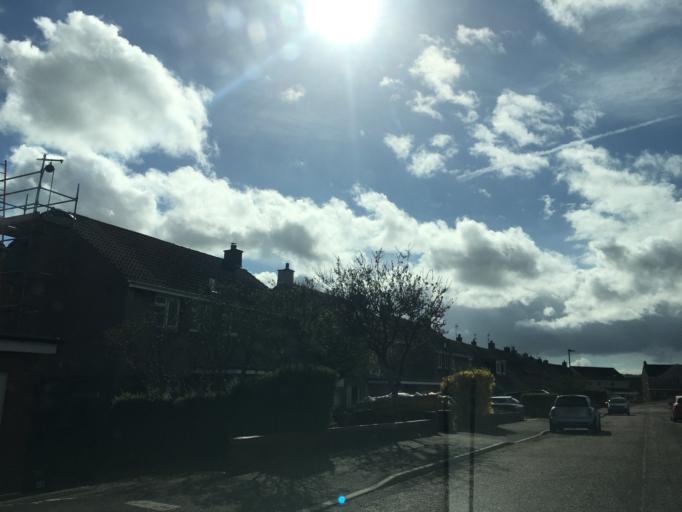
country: GB
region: Scotland
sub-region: Edinburgh
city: Colinton
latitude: 55.8992
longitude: -3.2101
